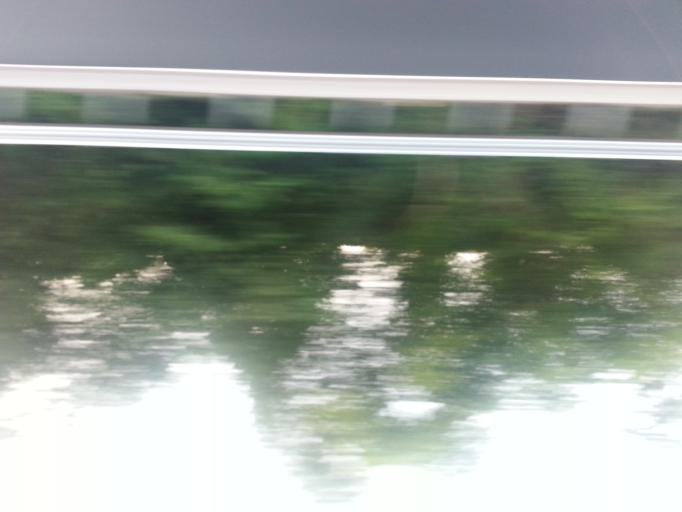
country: US
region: Tennessee
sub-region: Roane County
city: Kingston
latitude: 35.8728
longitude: -84.4966
